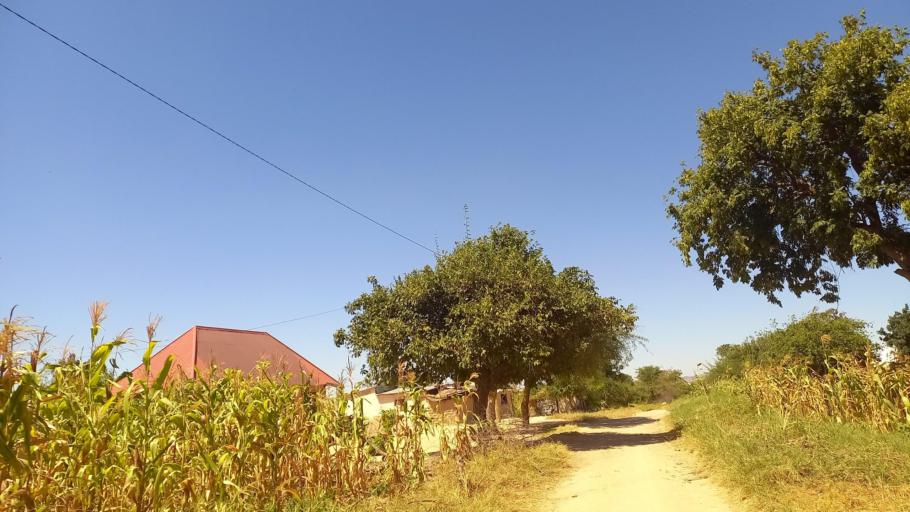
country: TZ
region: Dodoma
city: Dodoma
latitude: -6.1136
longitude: 35.6960
